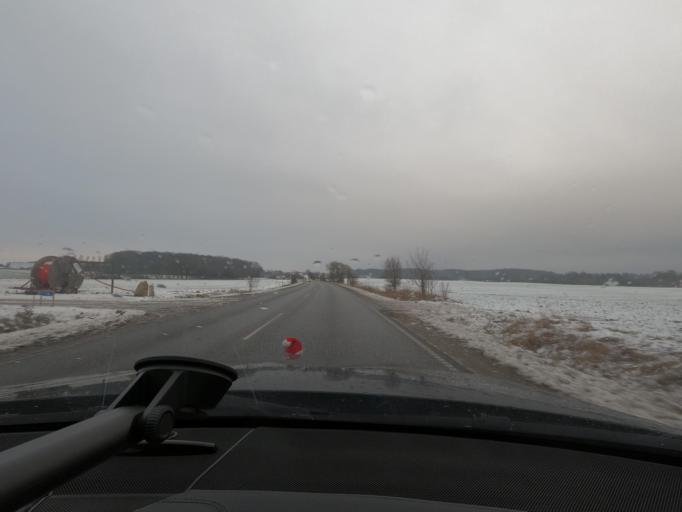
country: DK
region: South Denmark
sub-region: Sonderborg Kommune
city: Horuphav
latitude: 54.9233
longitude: 9.8748
